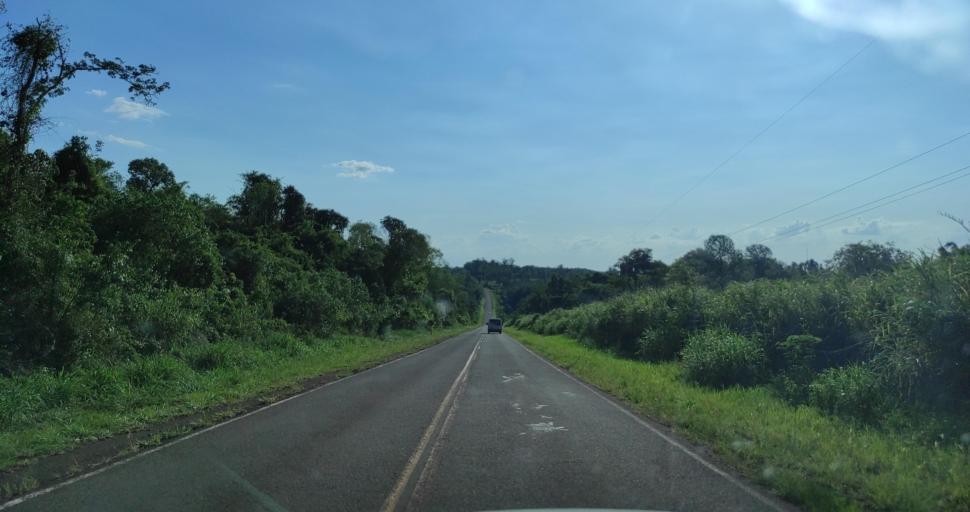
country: AR
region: Misiones
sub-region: Departamento de Eldorado
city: Eldorado
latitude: -26.3849
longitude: -54.3450
